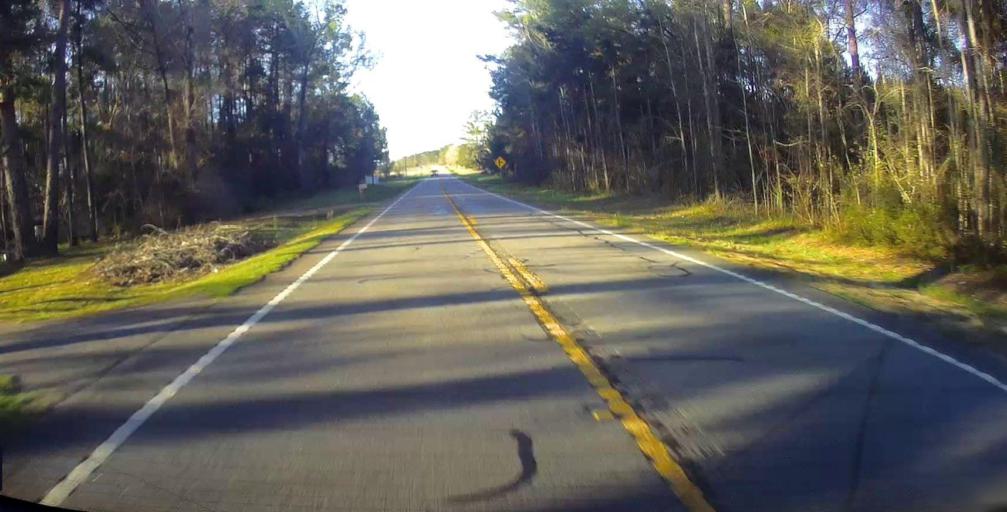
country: US
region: Georgia
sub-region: Wilcox County
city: Abbeville
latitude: 32.0185
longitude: -83.2496
